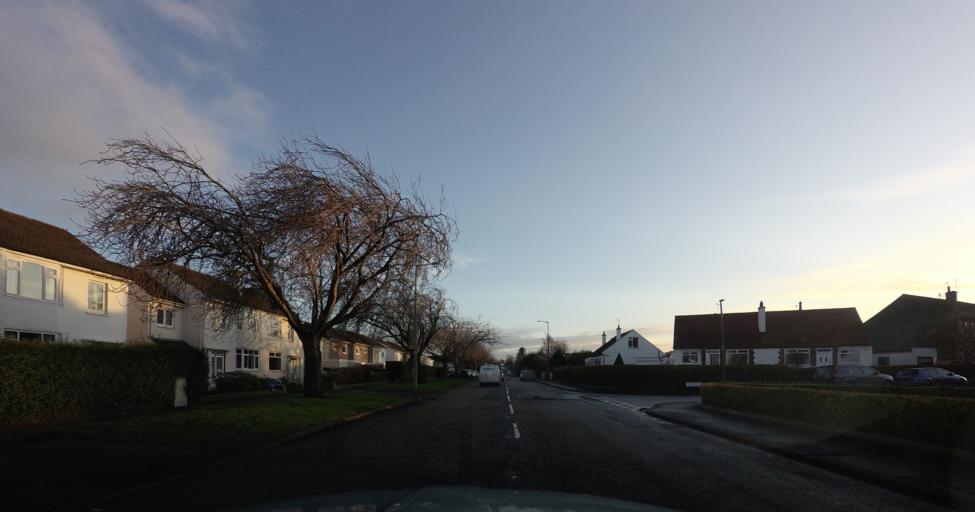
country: GB
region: Scotland
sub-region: Edinburgh
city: Colinton
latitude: 55.9712
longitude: -3.2719
